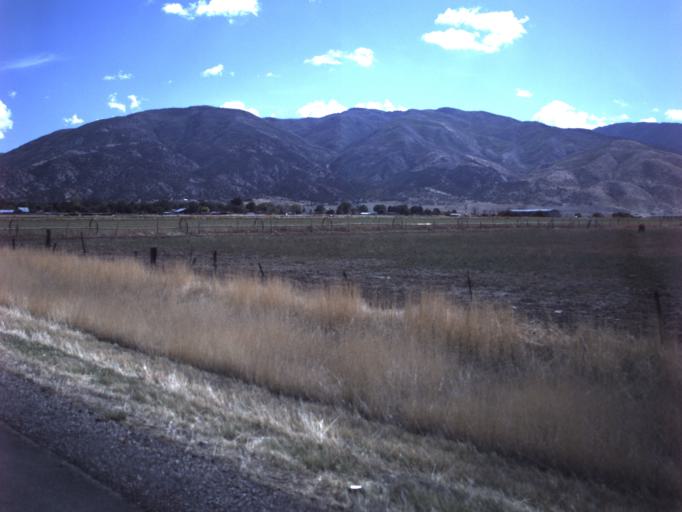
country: US
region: Utah
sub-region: Juab County
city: Nephi
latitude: 39.5583
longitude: -111.8817
